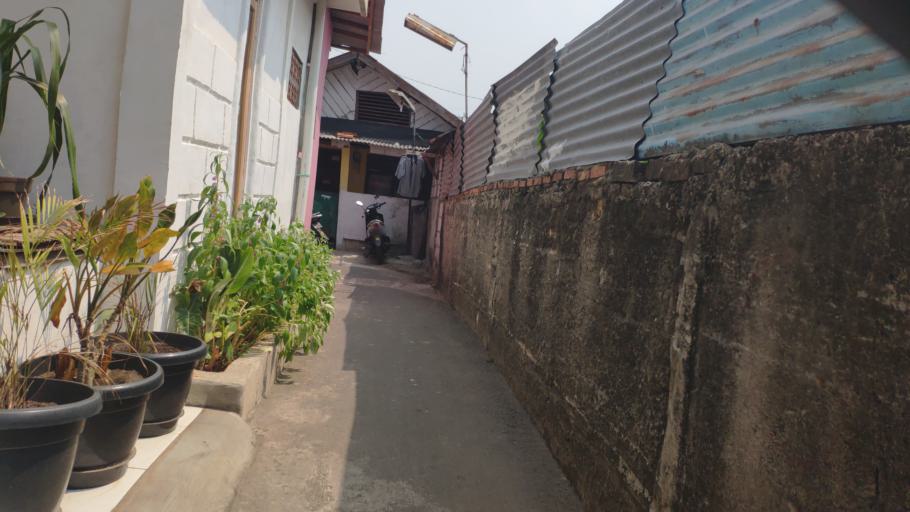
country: ID
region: Jakarta Raya
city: Jakarta
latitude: -6.2569
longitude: 106.7960
